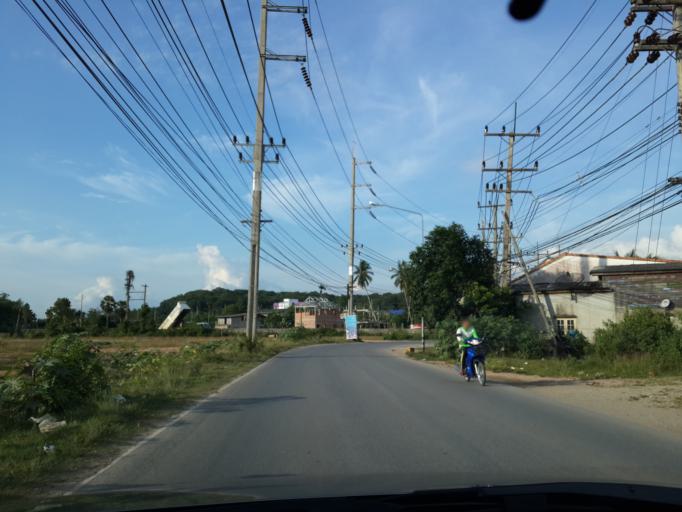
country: TH
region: Yala
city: Yala
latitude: 6.5113
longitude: 101.2707
